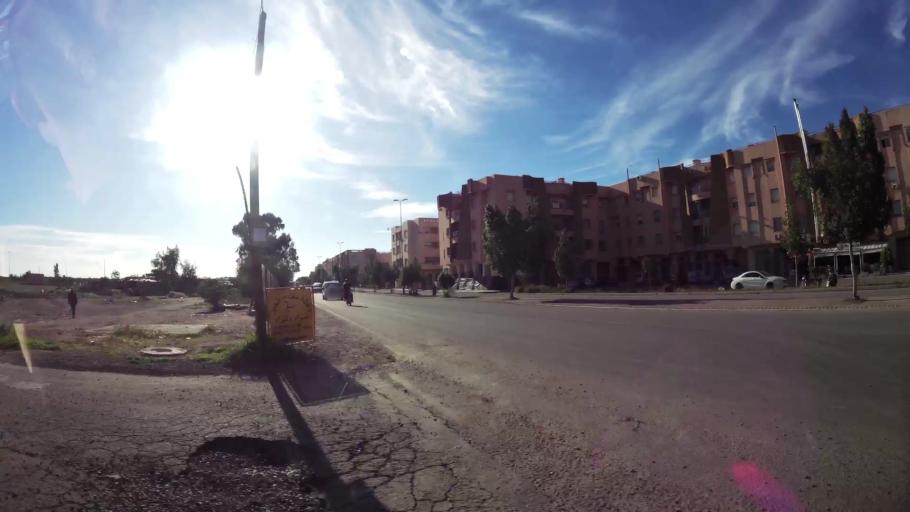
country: MA
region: Marrakech-Tensift-Al Haouz
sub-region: Marrakech
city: Marrakesh
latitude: 31.6826
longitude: -8.0625
